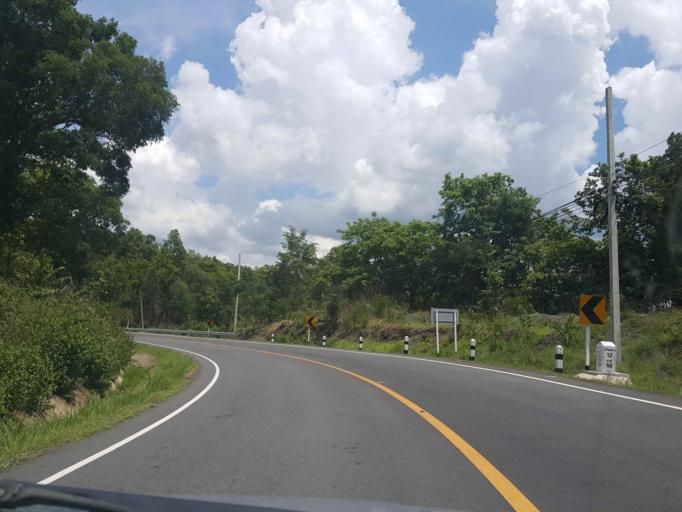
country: TH
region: Phayao
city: Chiang Muan
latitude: 18.8461
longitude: 100.3435
